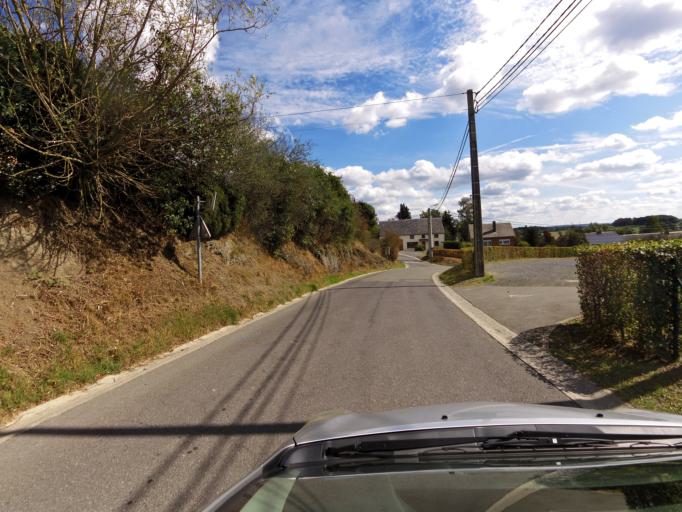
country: BE
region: Wallonia
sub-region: Province de Namur
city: Somme-Leuze
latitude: 50.3385
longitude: 5.3723
